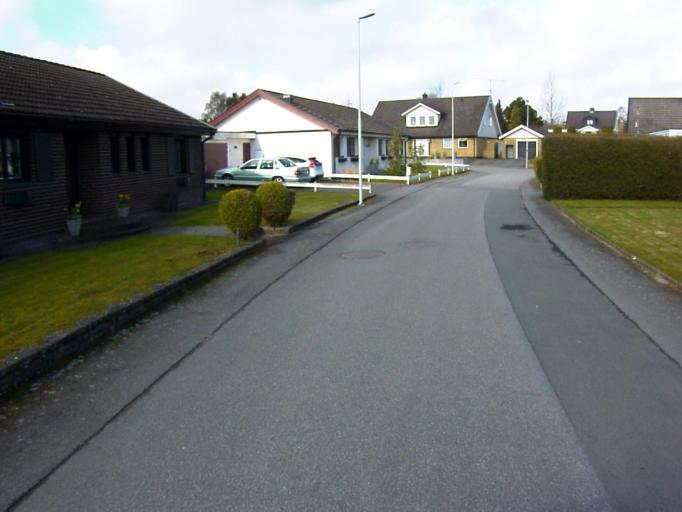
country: SE
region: Skane
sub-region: Kristianstads Kommun
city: Kristianstad
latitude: 56.0118
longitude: 14.1040
